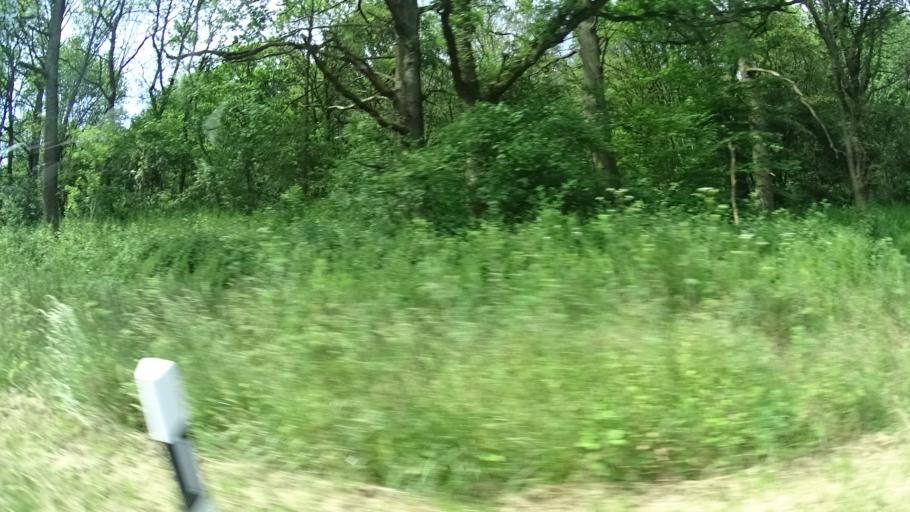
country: DE
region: Bavaria
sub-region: Regierungsbezirk Unterfranken
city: Faulbach
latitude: 49.7734
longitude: 9.4628
